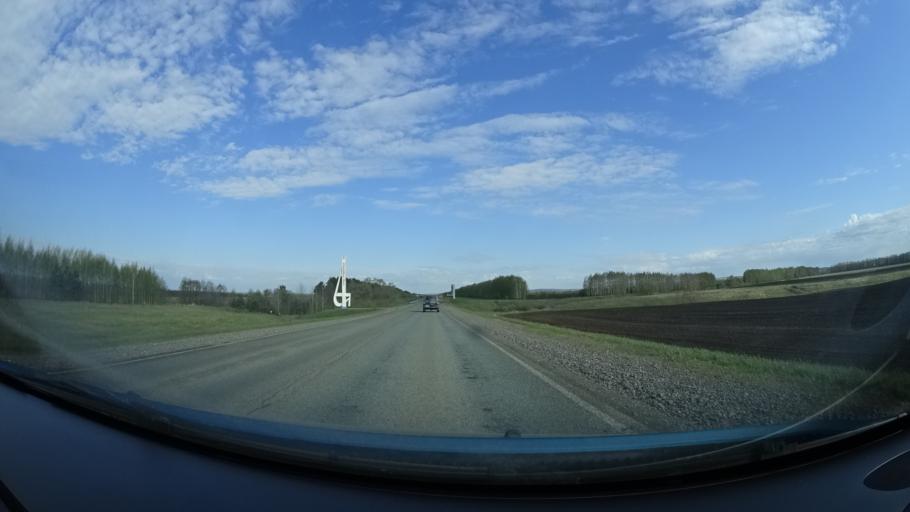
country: RU
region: Bashkortostan
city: Blagoveshchensk
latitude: 55.2171
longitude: 55.8030
